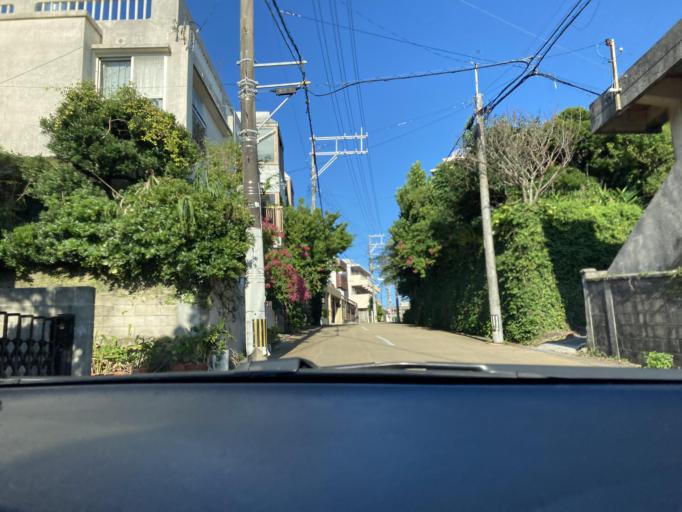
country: JP
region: Okinawa
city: Naha-shi
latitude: 26.2189
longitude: 127.7110
